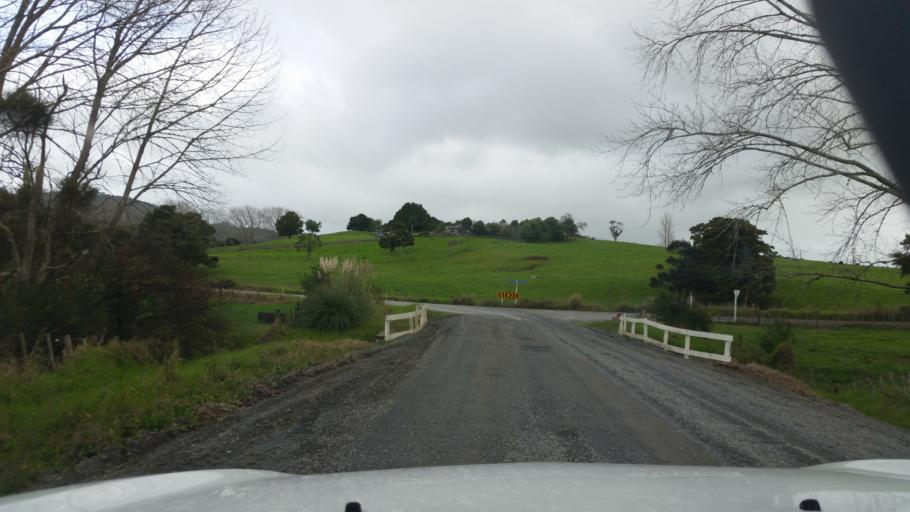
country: NZ
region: Northland
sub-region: Whangarei
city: Maungatapere
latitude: -35.6291
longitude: 174.1969
